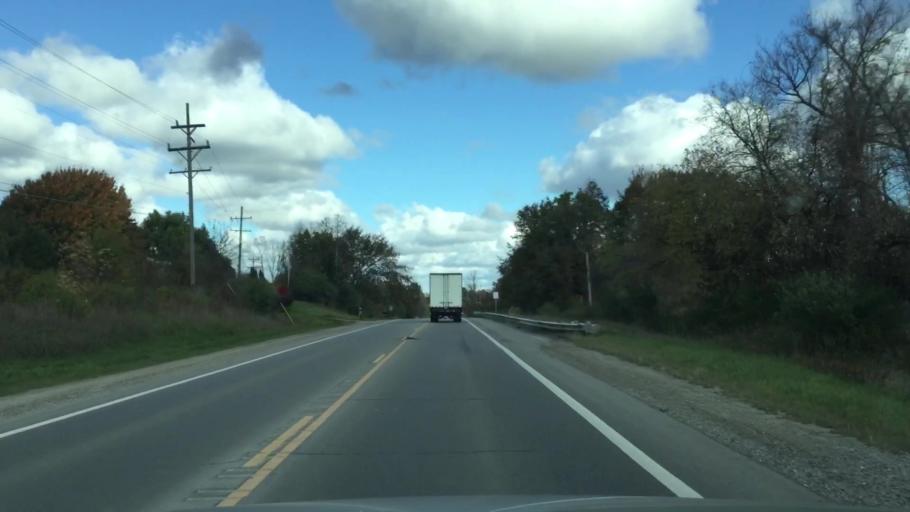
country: US
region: Michigan
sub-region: Oakland County
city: Oxford
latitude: 42.9080
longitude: -83.3122
